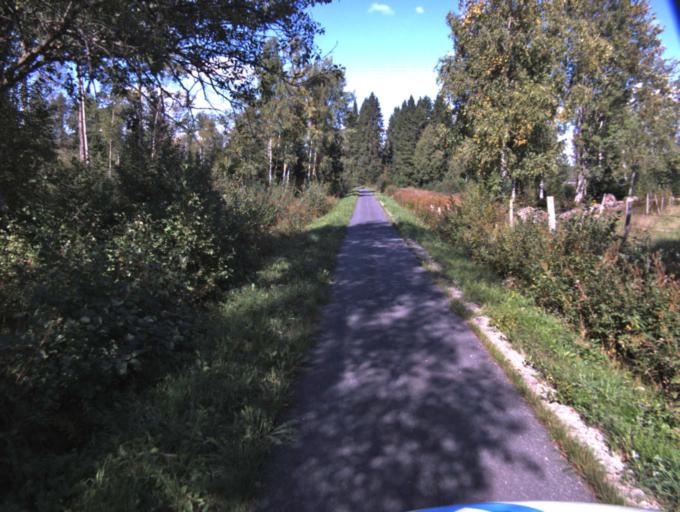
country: SE
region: Vaestra Goetaland
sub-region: Ulricehamns Kommun
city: Ulricehamn
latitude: 57.8130
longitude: 13.3545
